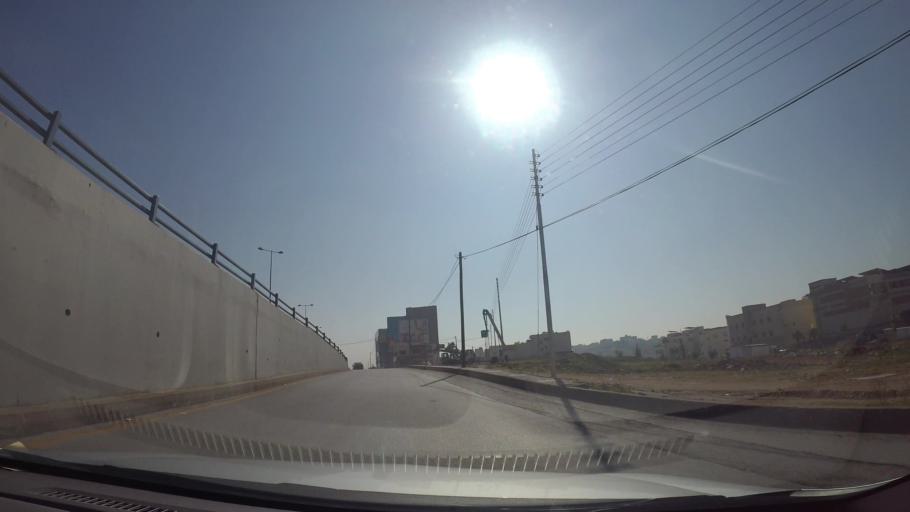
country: JO
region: Amman
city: Al Bunayyat ash Shamaliyah
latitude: 31.9185
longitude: 35.8978
